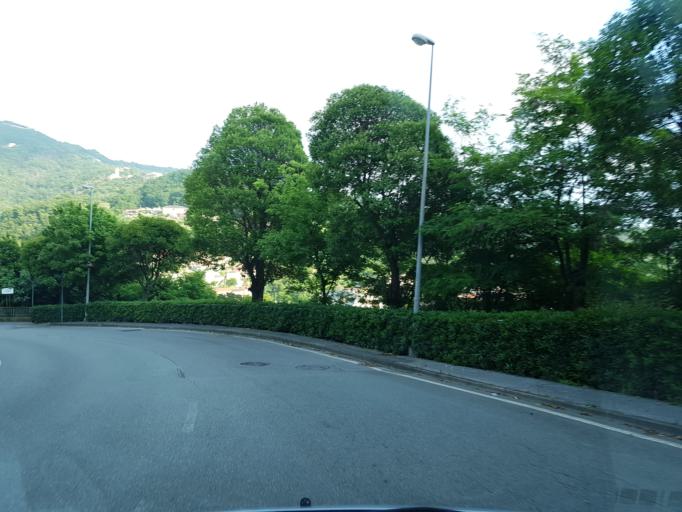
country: IT
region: Liguria
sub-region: Provincia di Genova
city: Genoa
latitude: 44.4428
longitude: 8.9005
